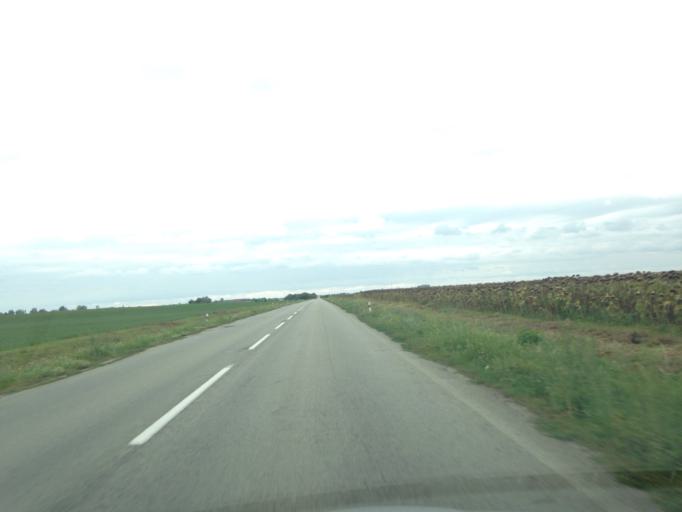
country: SK
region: Nitriansky
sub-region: Okres Komarno
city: Hurbanovo
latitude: 47.9041
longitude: 18.3429
